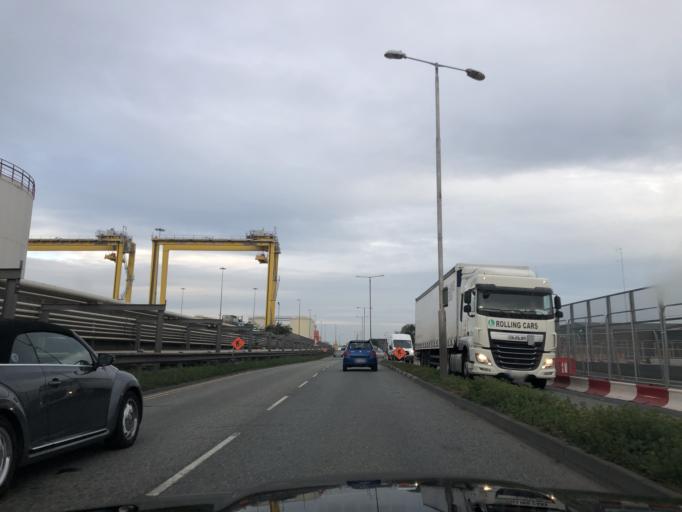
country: IE
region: Leinster
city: Sandymount
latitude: 53.3517
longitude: -6.2099
